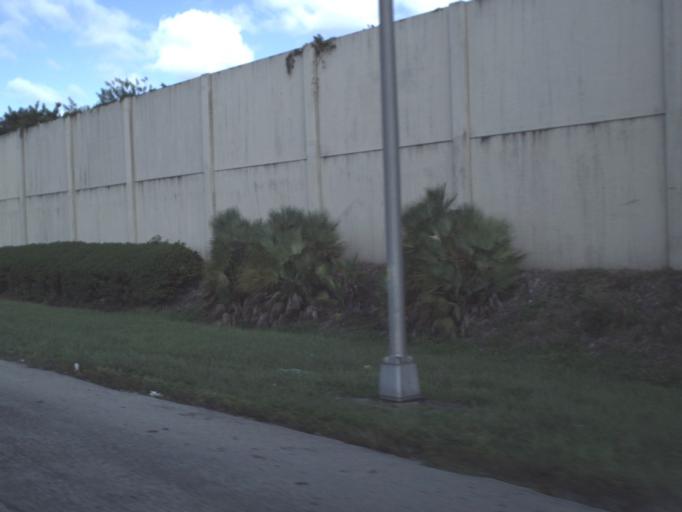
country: US
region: Florida
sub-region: Broward County
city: Parkland
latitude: 26.3007
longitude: -80.2125
